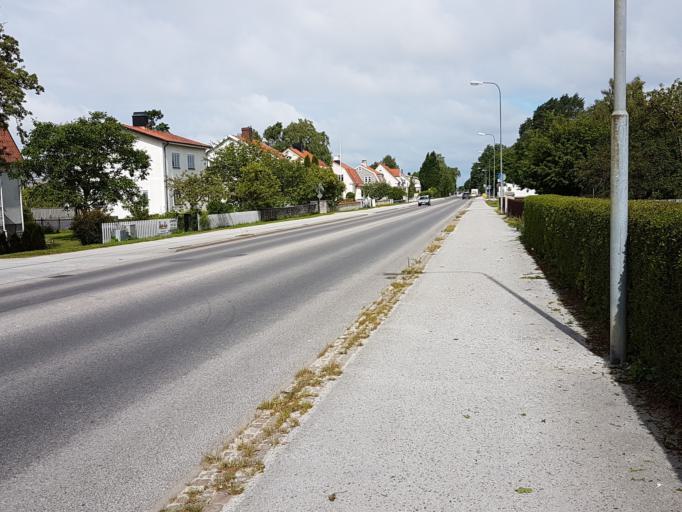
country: SE
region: Gotland
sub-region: Gotland
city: Visby
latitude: 57.6306
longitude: 18.3142
